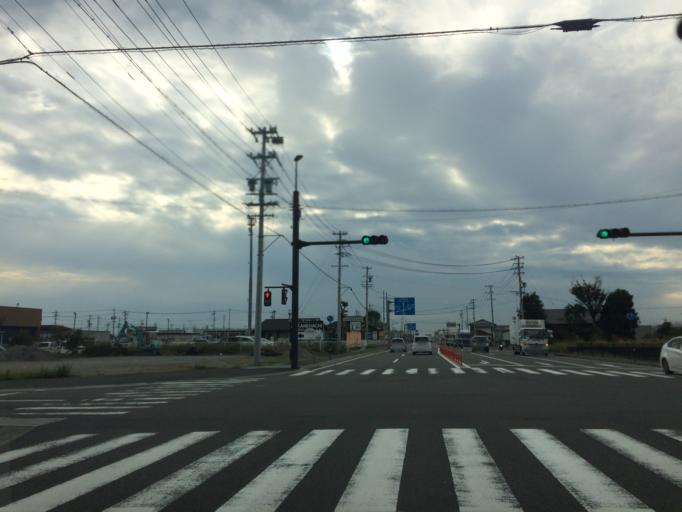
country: JP
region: Shizuoka
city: Shimada
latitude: 34.7802
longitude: 138.2525
